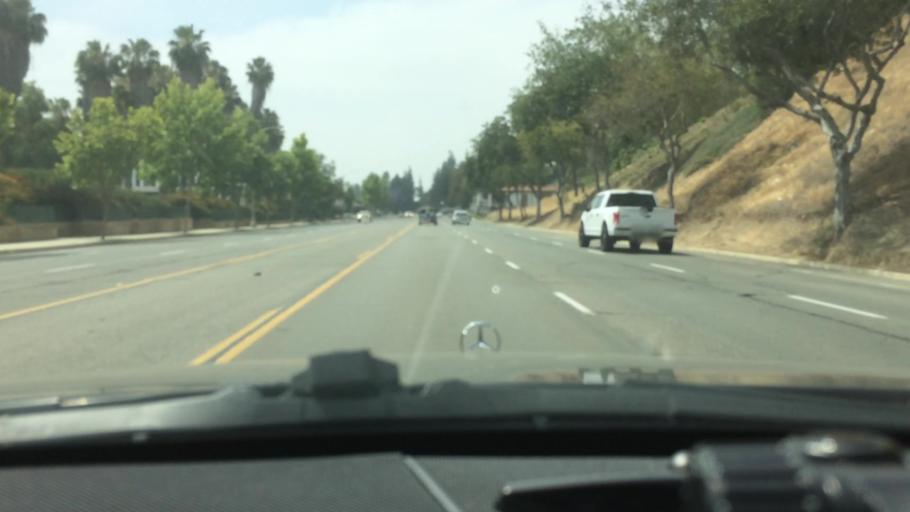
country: US
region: California
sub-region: Orange County
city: Fullerton
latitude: 33.8878
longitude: -117.9270
